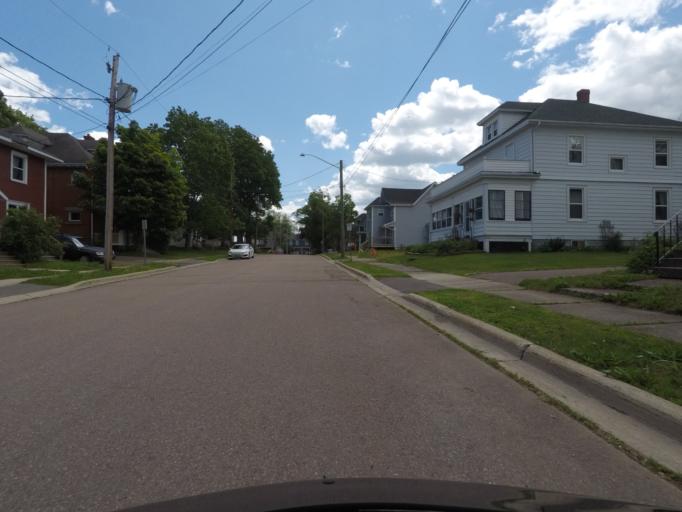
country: CA
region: New Brunswick
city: Moncton
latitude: 46.0952
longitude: -64.7888
